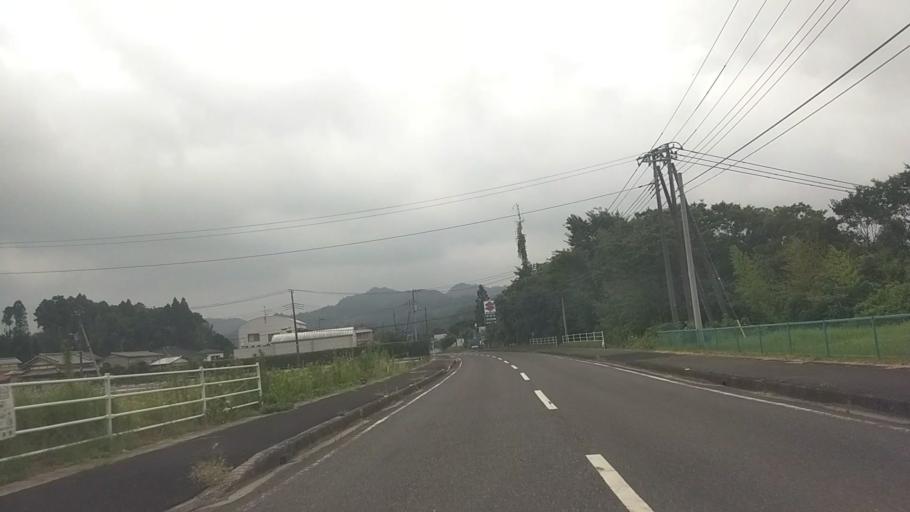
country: JP
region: Chiba
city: Kawaguchi
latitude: 35.2332
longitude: 140.0867
